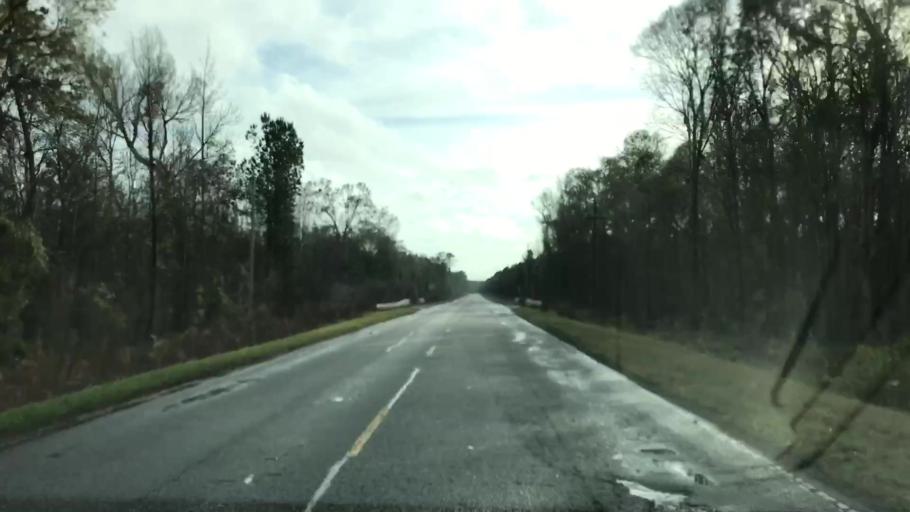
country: US
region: South Carolina
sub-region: Williamsburg County
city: Andrews
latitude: 33.4332
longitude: -79.5932
